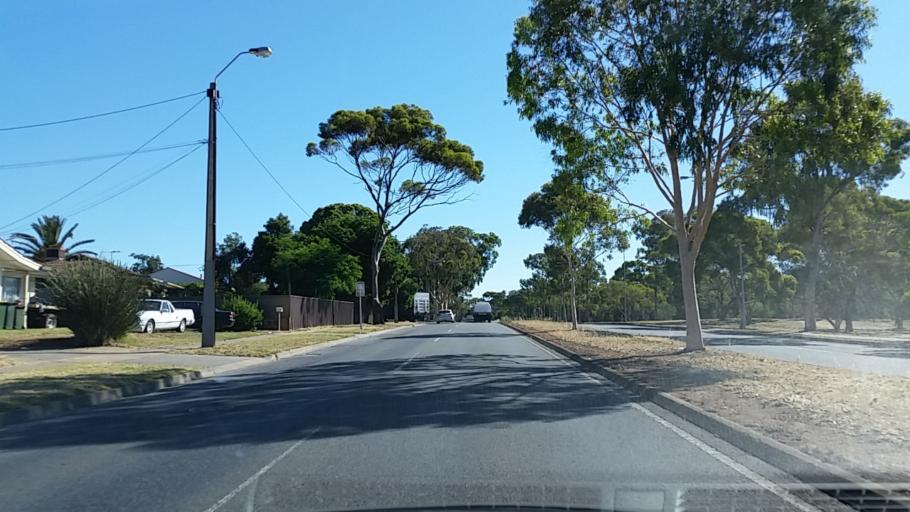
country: AU
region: South Australia
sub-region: Salisbury
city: Ingle Farm
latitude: -34.8129
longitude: 138.6438
